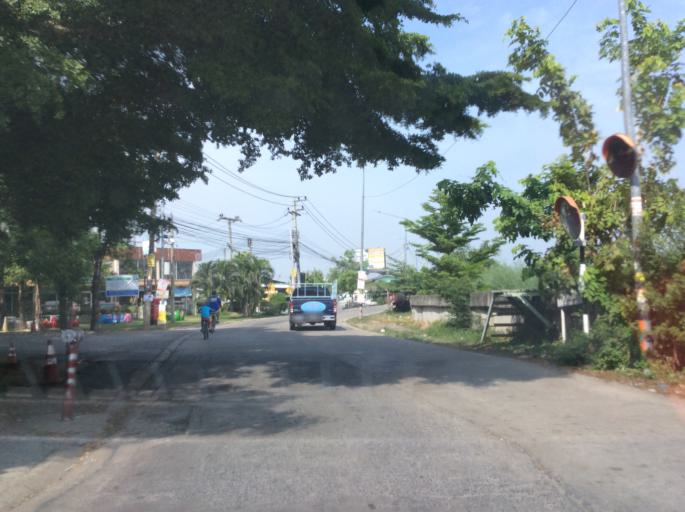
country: TH
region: Pathum Thani
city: Thanyaburi
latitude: 14.0112
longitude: 100.7147
